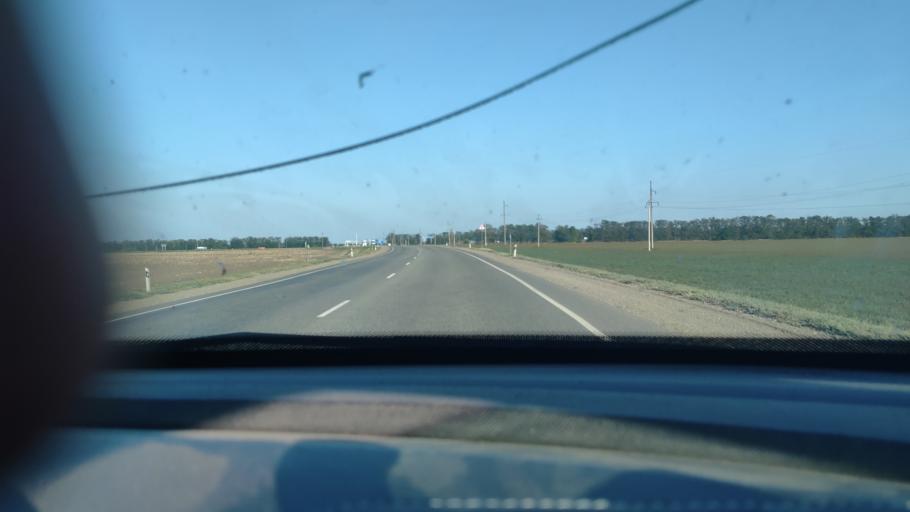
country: RU
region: Krasnodarskiy
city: Staroshcherbinovskaya
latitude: 46.6107
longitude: 38.6432
